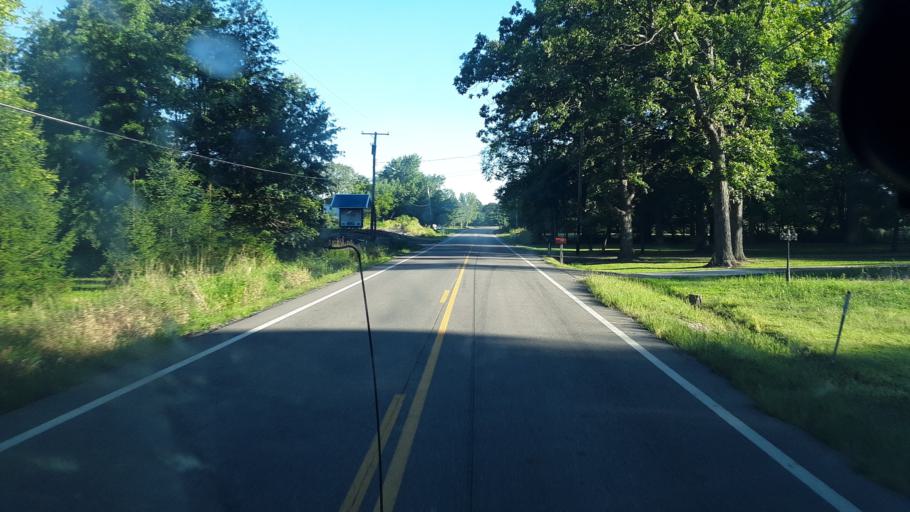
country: US
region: Ohio
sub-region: Trumbull County
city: Leavittsburg
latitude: 41.3244
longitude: -80.9566
